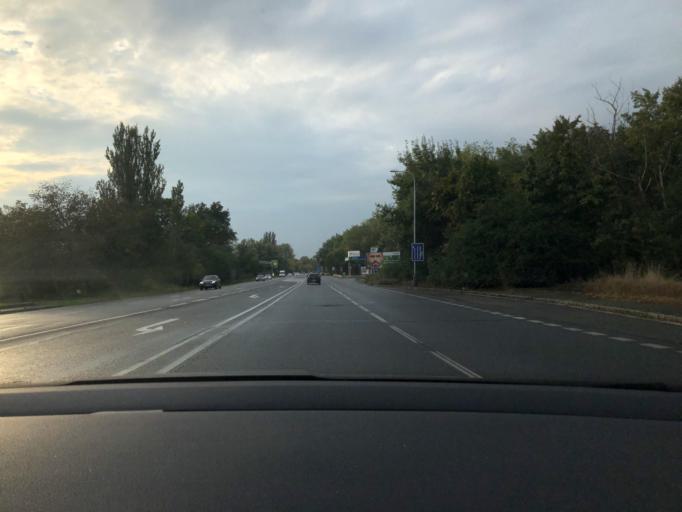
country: CZ
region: Central Bohemia
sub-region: Okres Kolin
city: Kolin
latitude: 50.0321
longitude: 15.1815
